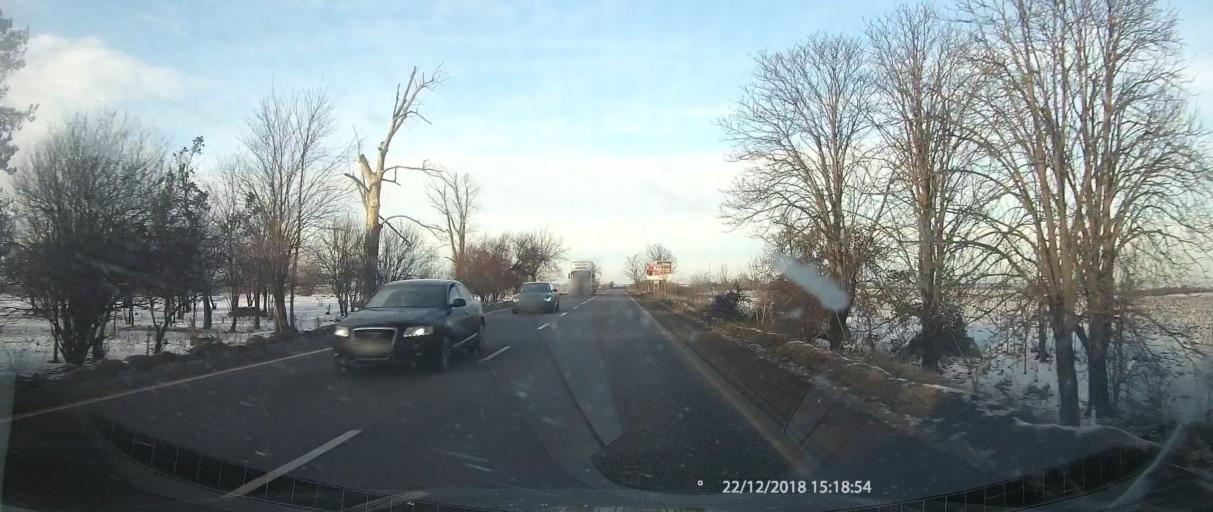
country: BG
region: Ruse
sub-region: Obshtina Dve Mogili
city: Dve Mogili
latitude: 43.6456
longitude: 25.8726
